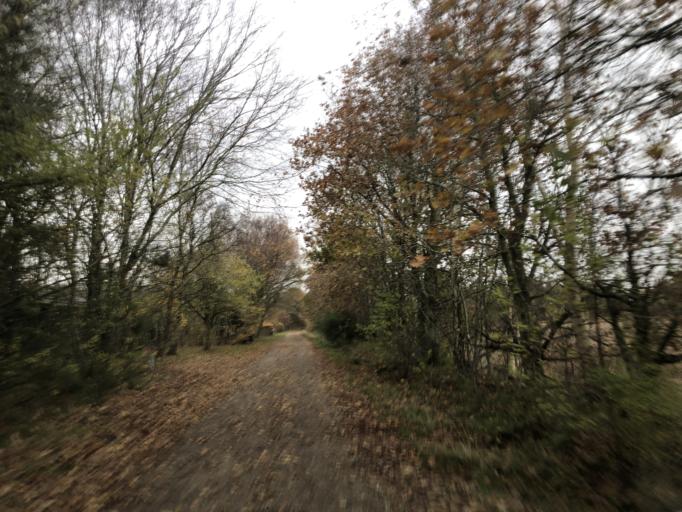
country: DK
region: Central Jutland
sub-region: Holstebro Kommune
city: Ulfborg
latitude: 56.3174
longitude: 8.2171
